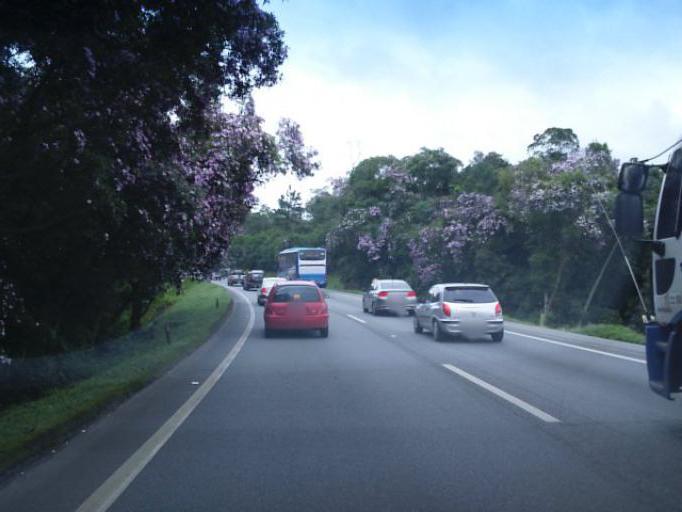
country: BR
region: Parana
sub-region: Guaratuba
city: Guaratuba
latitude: -25.9266
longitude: -48.9123
